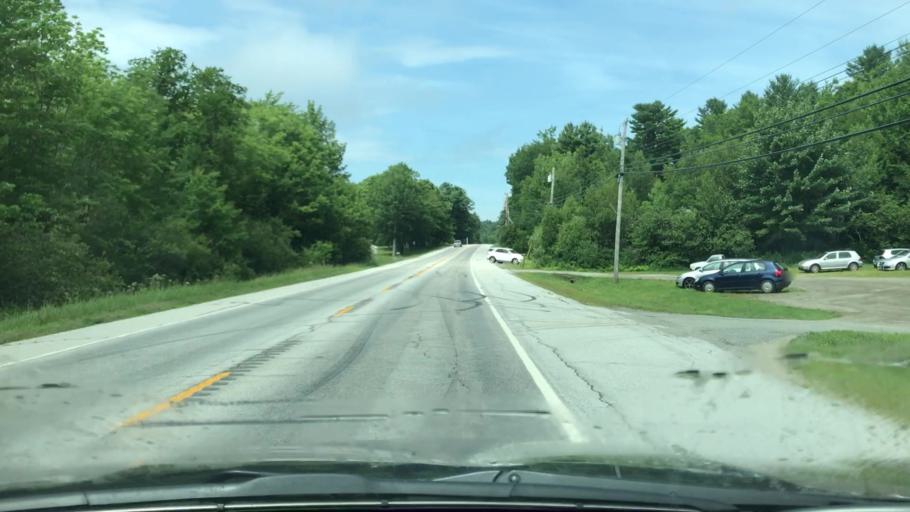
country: US
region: Maine
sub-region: Waldo County
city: Northport
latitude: 44.3474
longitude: -68.9693
